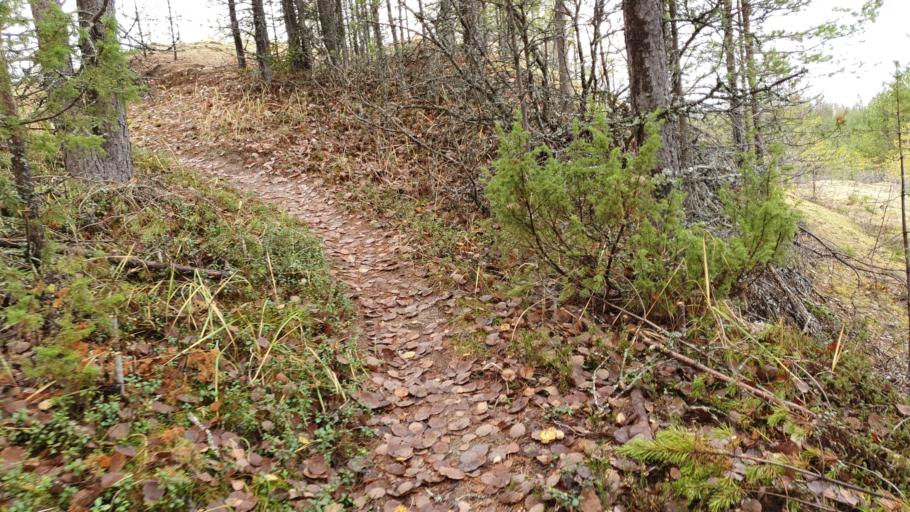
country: FI
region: Kainuu
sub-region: Kehys-Kainuu
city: Kuhmo
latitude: 64.1514
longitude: 29.3965
